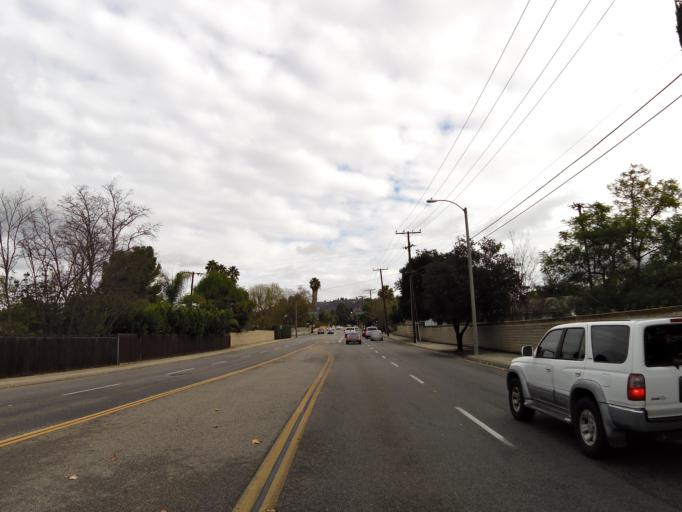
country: US
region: California
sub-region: Ventura County
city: Thousand Oaks
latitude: 34.1995
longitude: -118.8655
